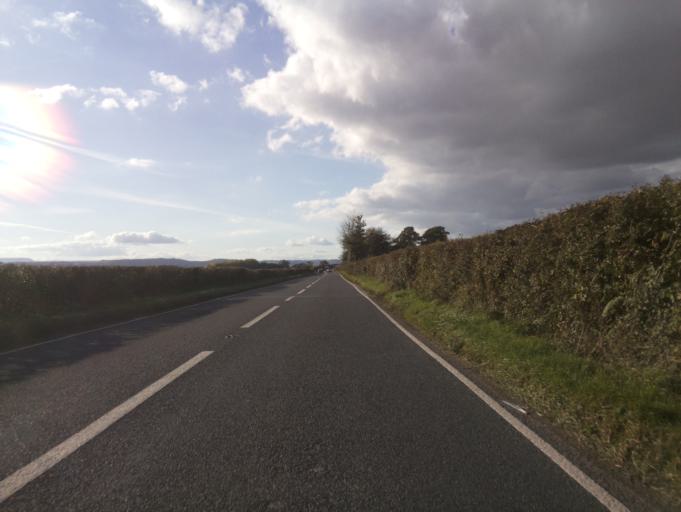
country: GB
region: England
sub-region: Herefordshire
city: Bridge Sollers
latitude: 52.0745
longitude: -2.8346
